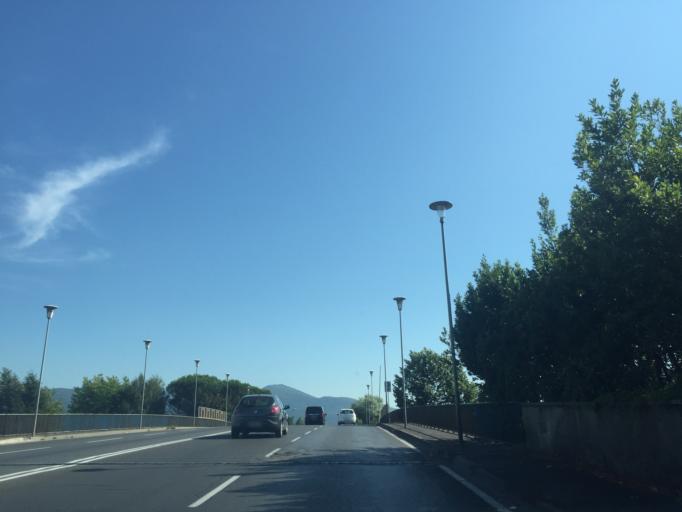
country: IT
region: Tuscany
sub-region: Provincia di Lucca
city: Lucca
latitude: 43.8384
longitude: 10.4951
